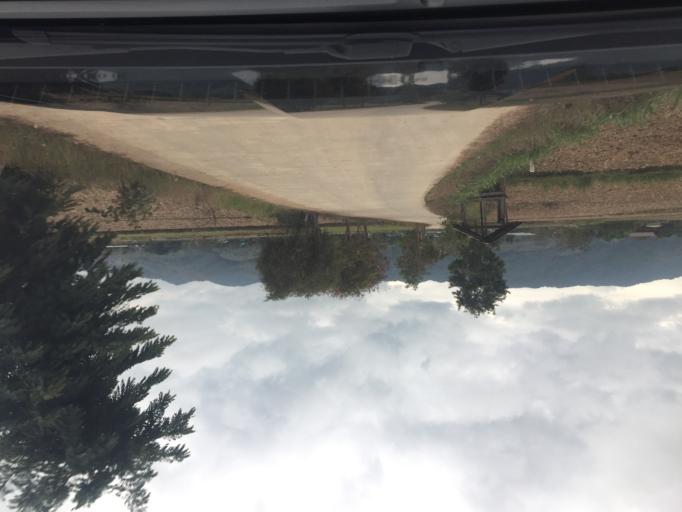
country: TH
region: Phayao
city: Pong
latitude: 19.1632
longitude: 100.3152
